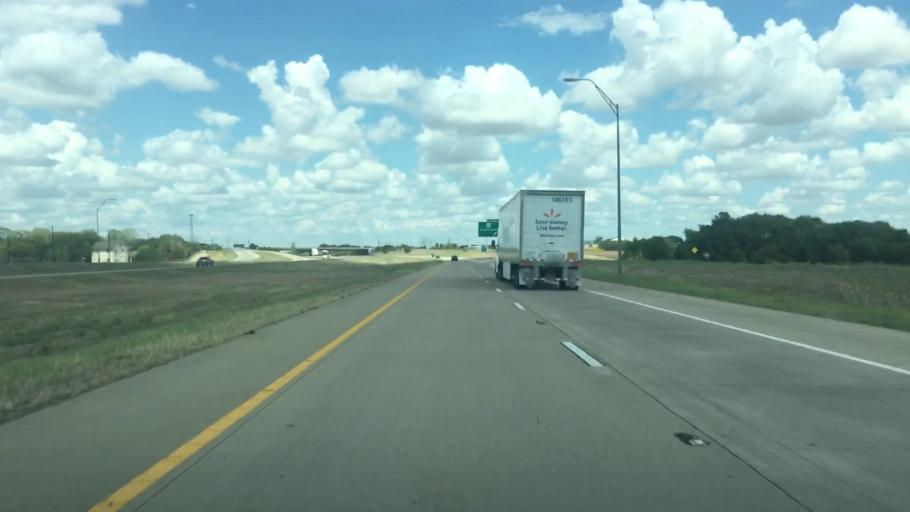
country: US
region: Texas
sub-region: Williamson County
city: Georgetown
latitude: 30.6342
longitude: -97.6280
